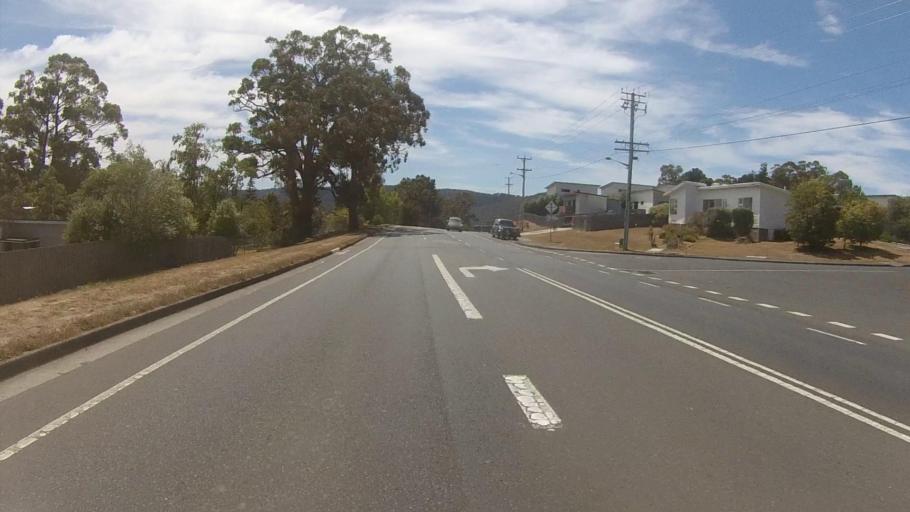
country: AU
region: Tasmania
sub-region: Kingborough
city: Kingston
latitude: -42.9799
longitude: 147.2989
